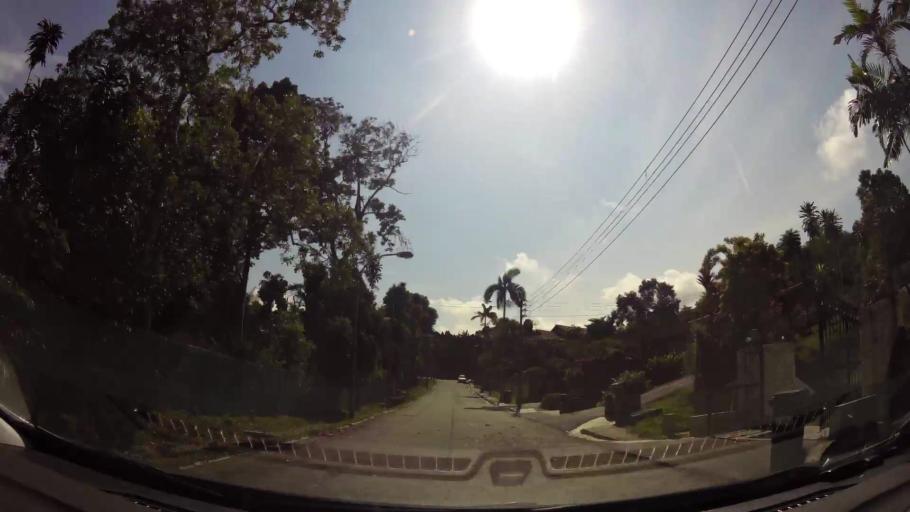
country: SG
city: Singapore
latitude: 1.3561
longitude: 103.8234
